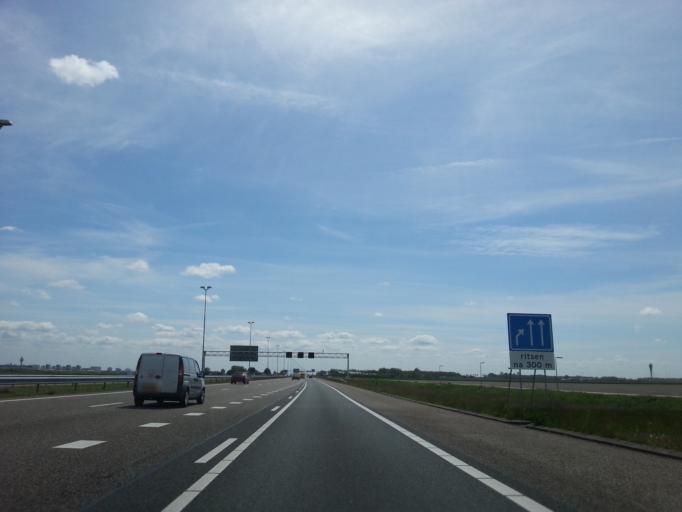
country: NL
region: North Holland
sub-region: Gemeente Haarlemmermeer
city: Hoofddorp
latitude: 52.3473
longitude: 4.7355
